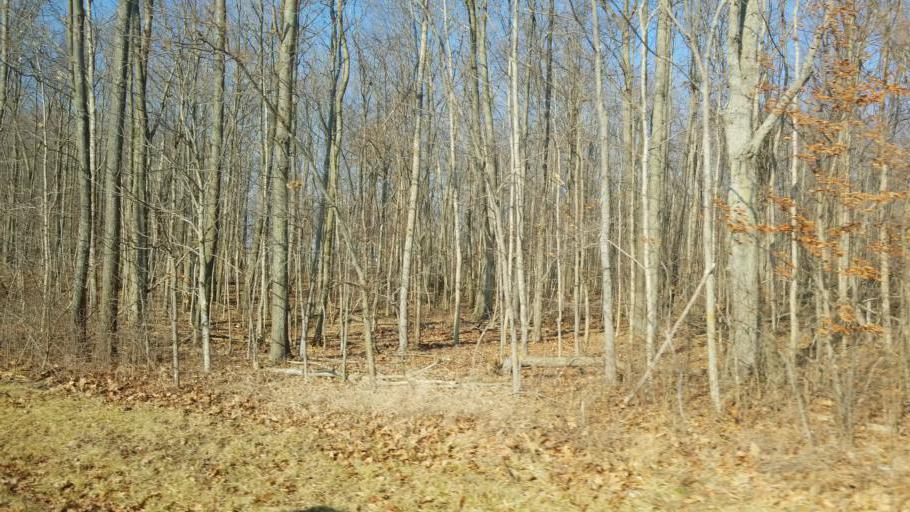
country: US
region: Ohio
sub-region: Seneca County
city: Tiffin
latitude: 41.0372
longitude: -83.0847
